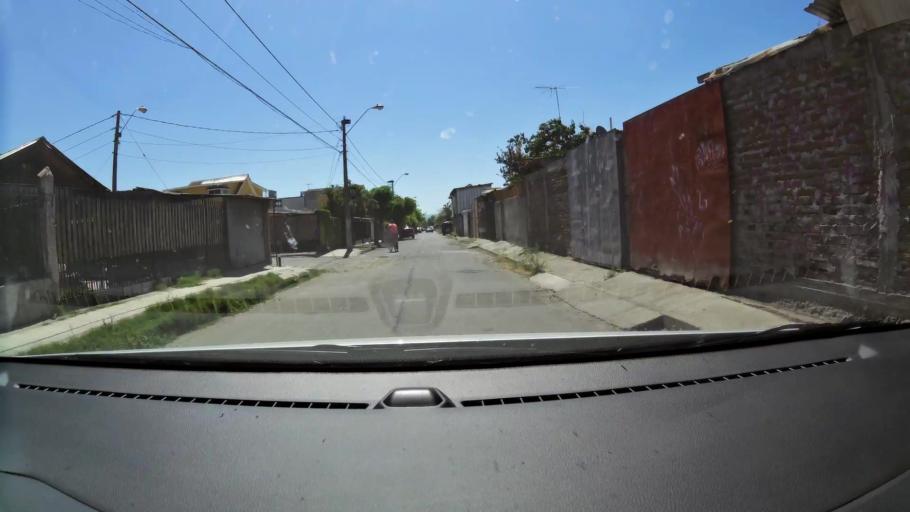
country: CL
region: Santiago Metropolitan
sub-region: Provincia de Maipo
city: San Bernardo
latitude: -33.5764
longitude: -70.6766
